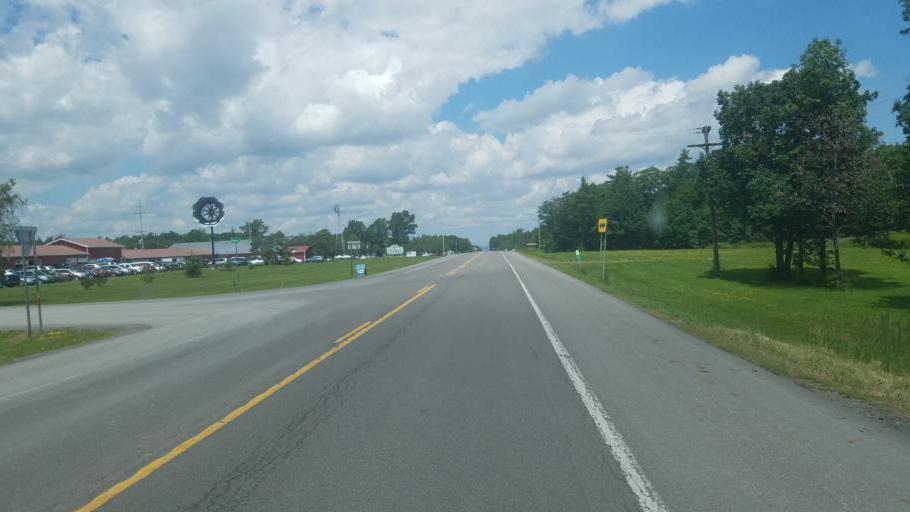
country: US
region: New York
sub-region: Yates County
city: Keuka Park
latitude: 42.5731
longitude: -77.0357
